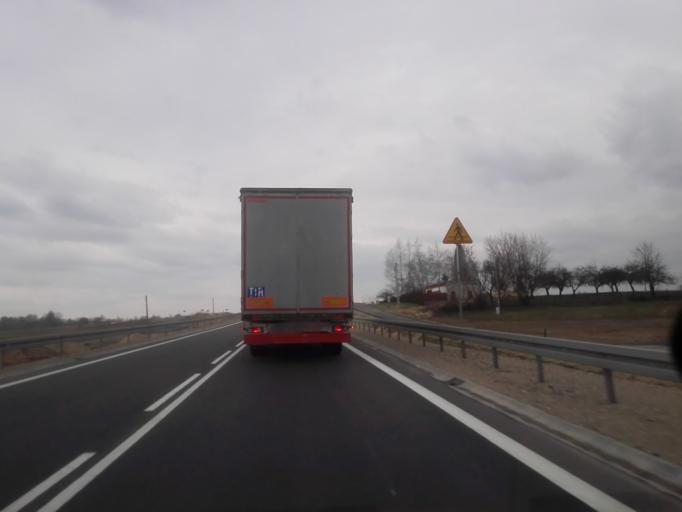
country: PL
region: Podlasie
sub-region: Powiat augustowski
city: Augustow
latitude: 53.7870
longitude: 22.8550
